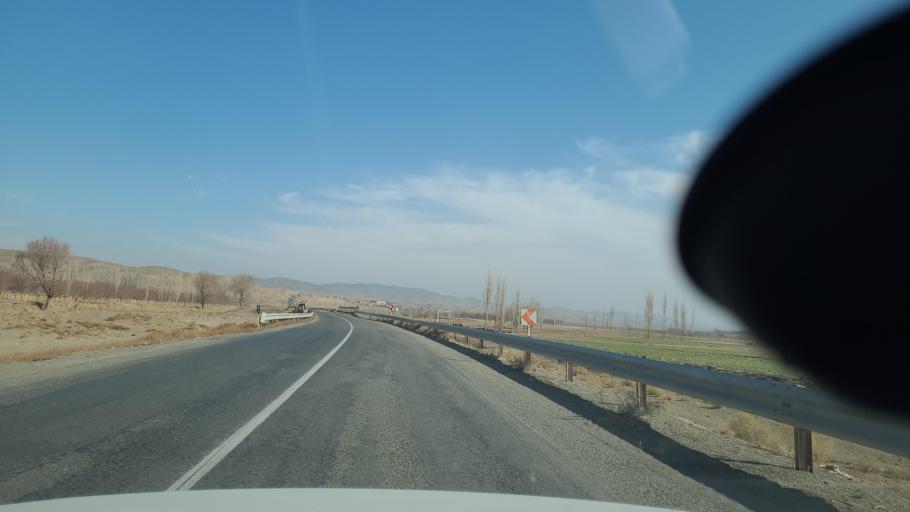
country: IR
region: Razavi Khorasan
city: Fariman
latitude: 35.5887
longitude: 59.6659
